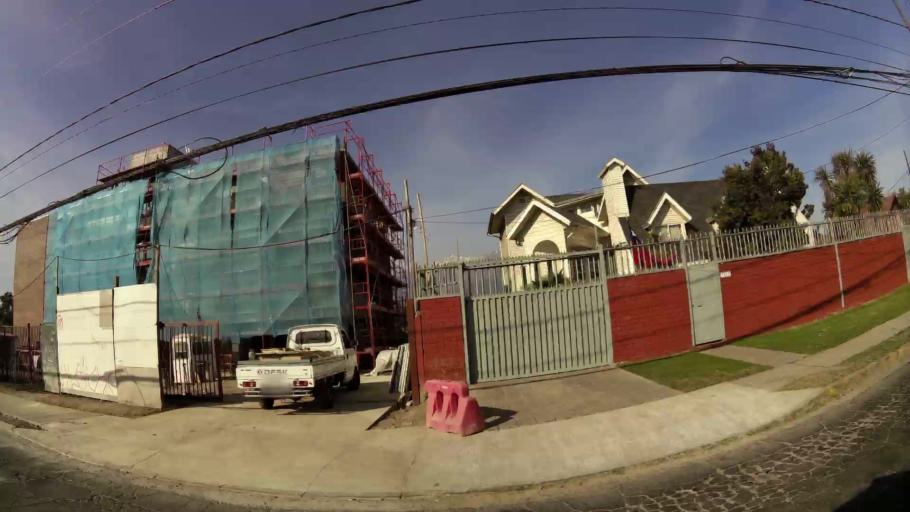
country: CL
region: Santiago Metropolitan
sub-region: Provincia de Santiago
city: La Pintana
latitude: -33.5378
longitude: -70.5840
